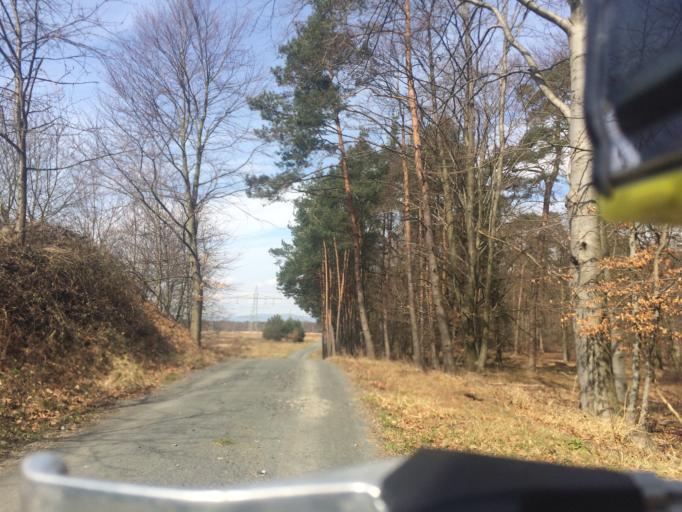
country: DE
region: Hesse
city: Kelsterbach
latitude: 50.0220
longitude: 8.5086
